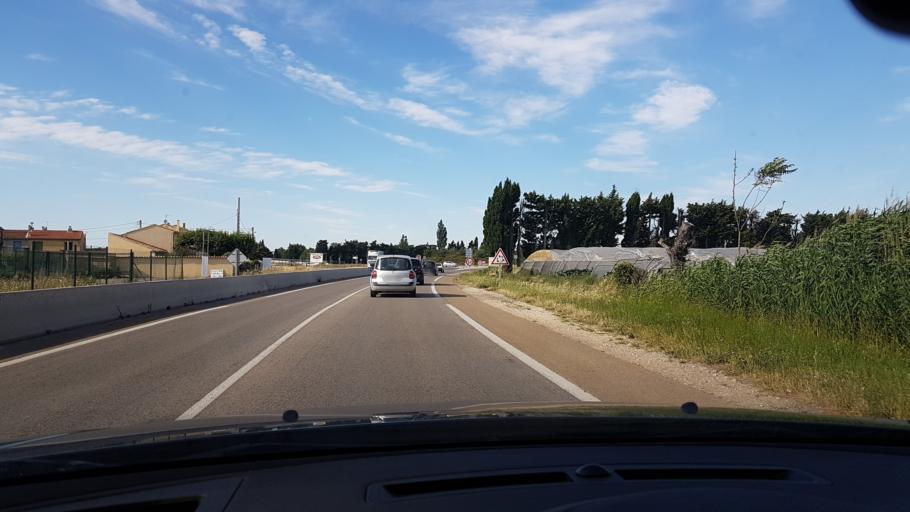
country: FR
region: Provence-Alpes-Cote d'Azur
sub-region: Departement des Bouches-du-Rhone
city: Rognonas
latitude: 43.8944
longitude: 4.7840
